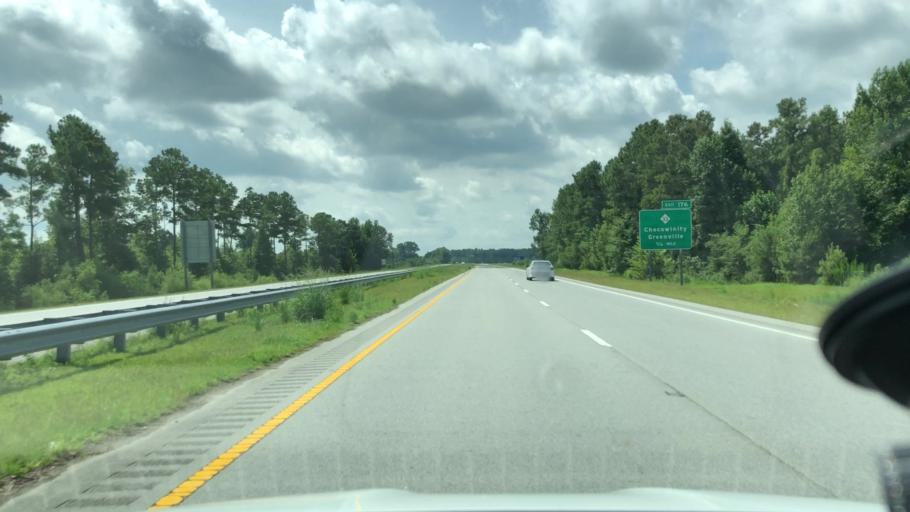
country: US
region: North Carolina
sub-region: Beaufort County
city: Washington
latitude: 35.5168
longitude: -77.0860
